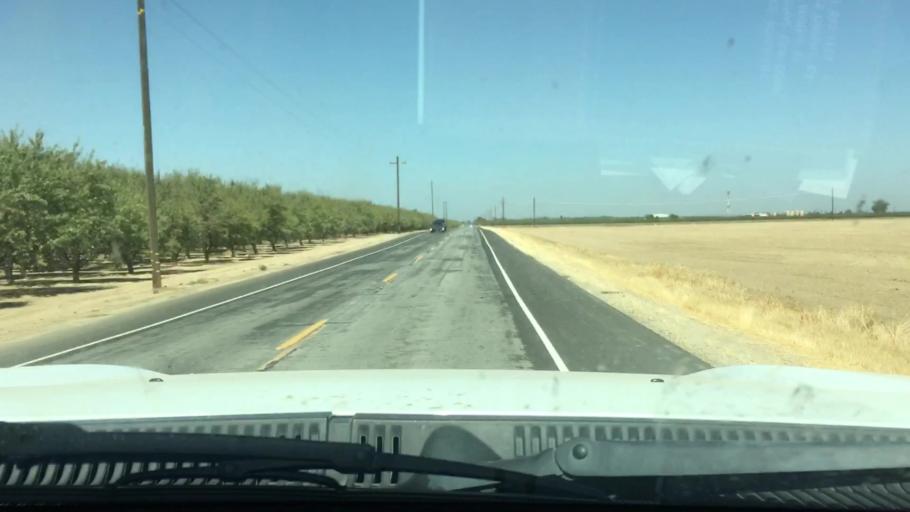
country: US
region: California
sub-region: Kern County
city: Shafter
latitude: 35.4454
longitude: -119.2789
